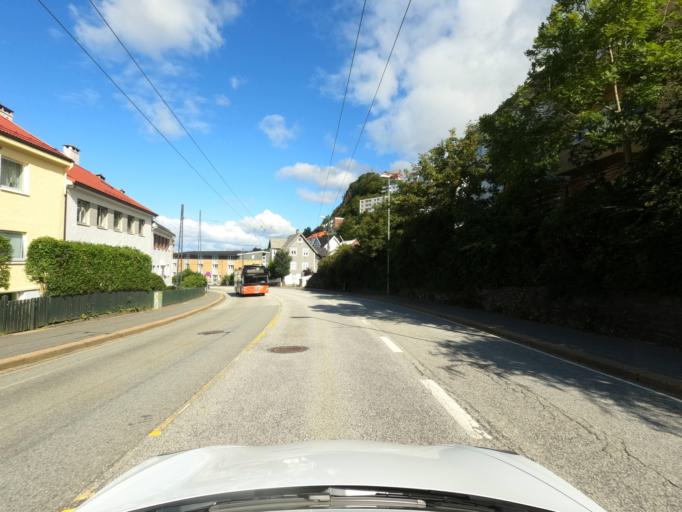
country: NO
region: Hordaland
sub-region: Bergen
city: Bergen
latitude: 60.3676
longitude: 5.3650
